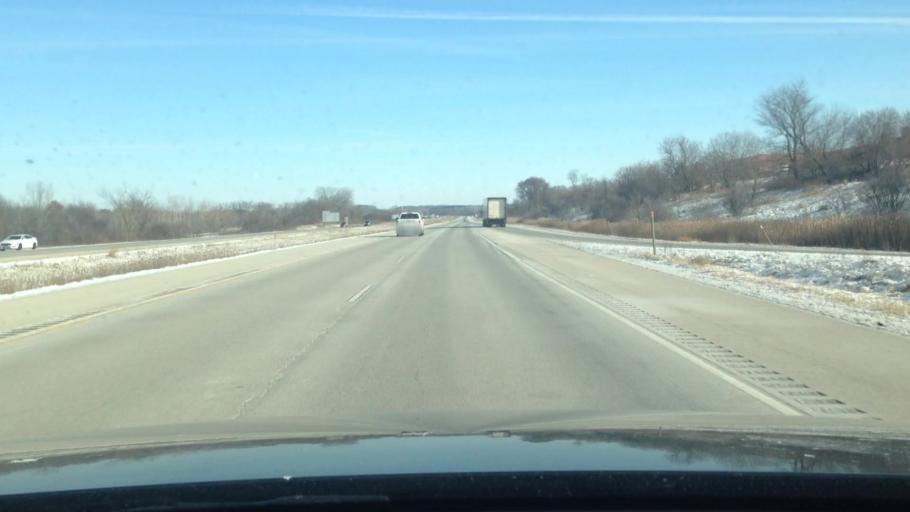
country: US
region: Wisconsin
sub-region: Waukesha County
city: Mukwonago
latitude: 42.8538
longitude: -88.3184
